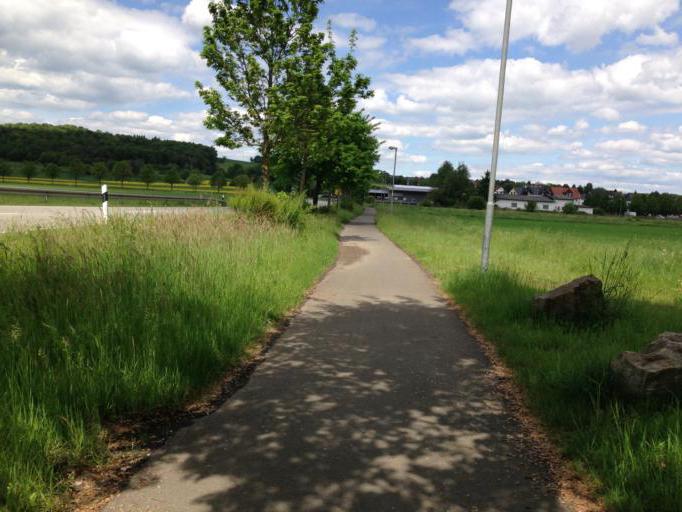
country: DE
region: Hesse
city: Lollar
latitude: 50.6572
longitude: 8.7071
